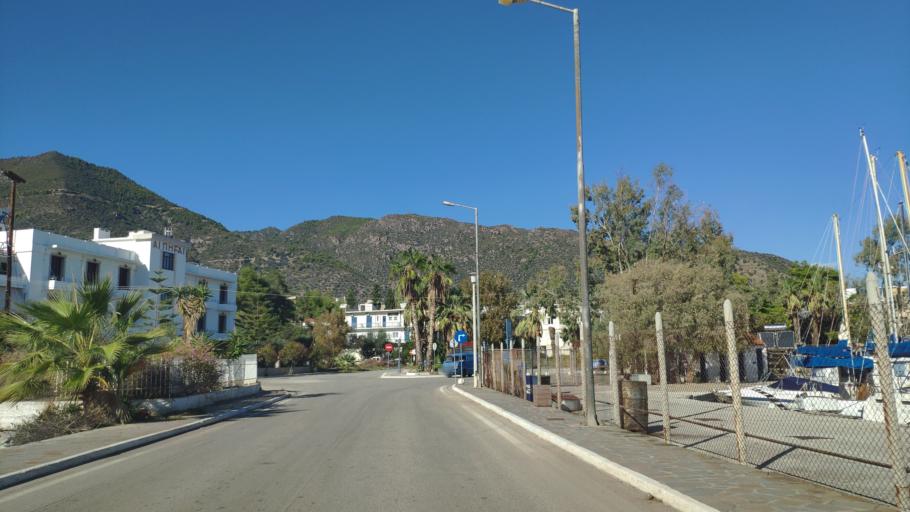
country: GR
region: Attica
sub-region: Nomos Piraios
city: Galatas
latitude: 37.5777
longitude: 23.3877
